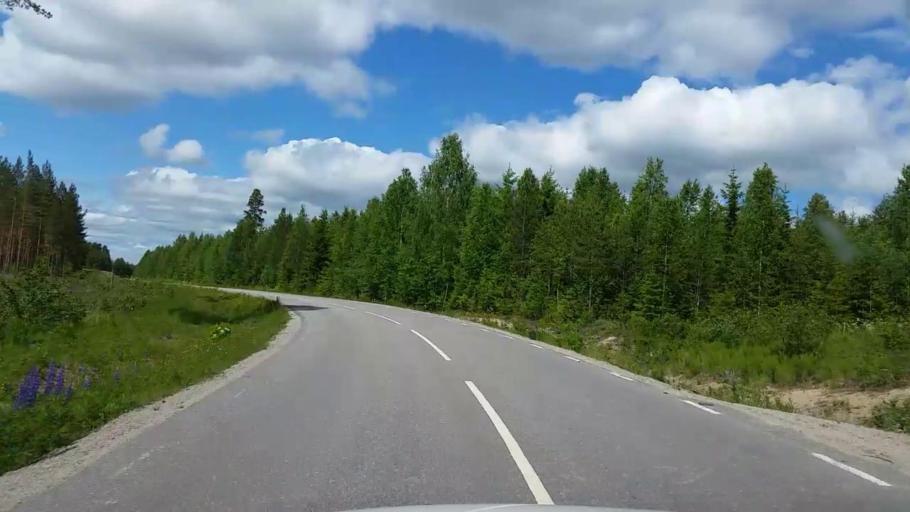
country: SE
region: Gaevleborg
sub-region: Ovanakers Kommun
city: Alfta
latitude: 61.2636
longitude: 16.1230
